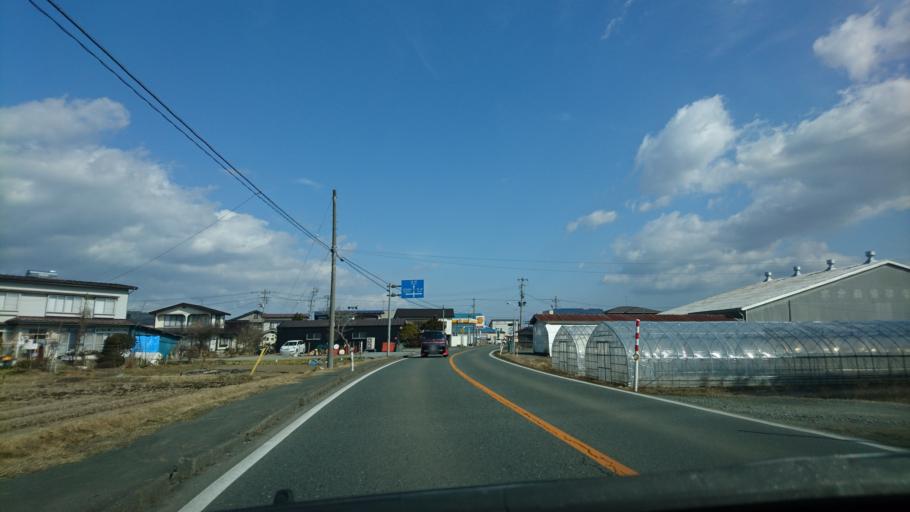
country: JP
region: Iwate
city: Morioka-shi
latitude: 39.5672
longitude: 141.1084
